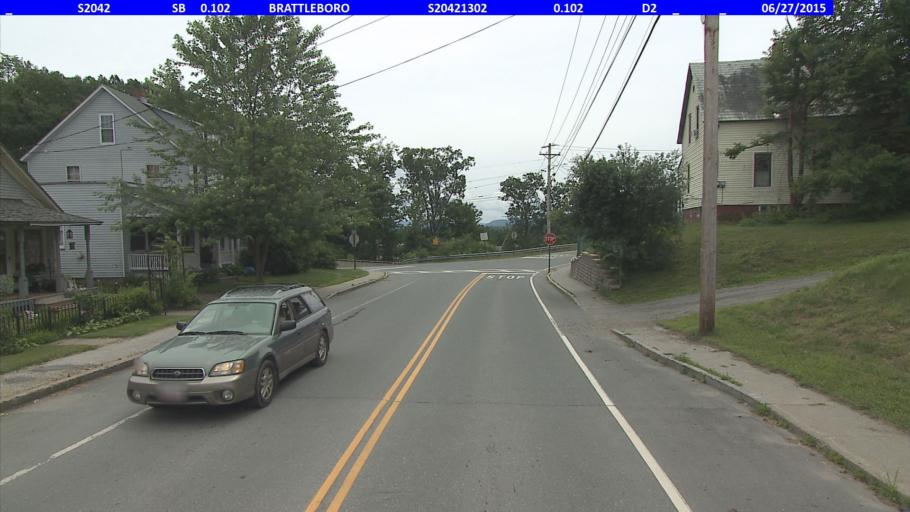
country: US
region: Vermont
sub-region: Windham County
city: Brattleboro
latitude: 42.8389
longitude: -72.5547
